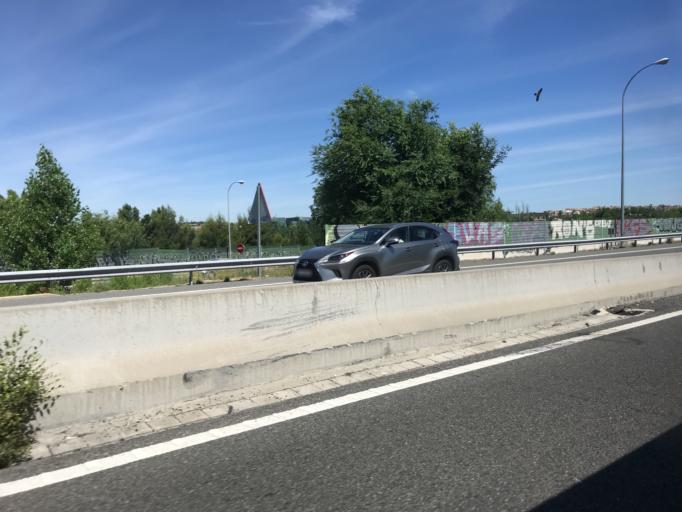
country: ES
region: Madrid
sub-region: Provincia de Madrid
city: San Blas
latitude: 40.4470
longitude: -3.5897
